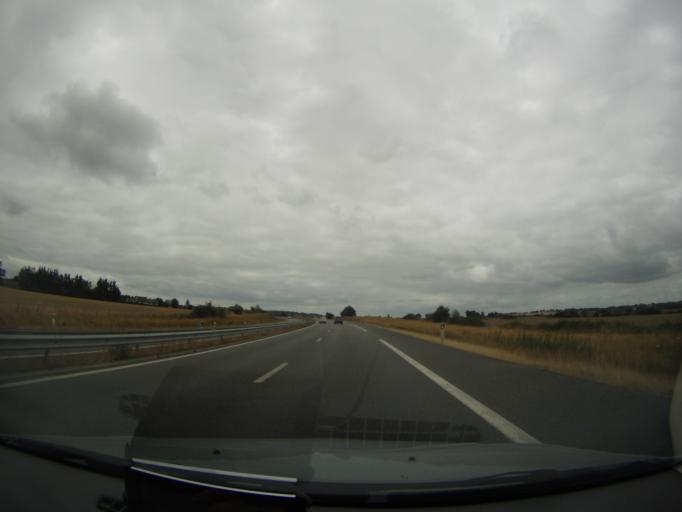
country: FR
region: Brittany
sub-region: Departement d'Ille-et-Vilaine
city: La Dominelais
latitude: 47.7727
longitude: -1.7071
